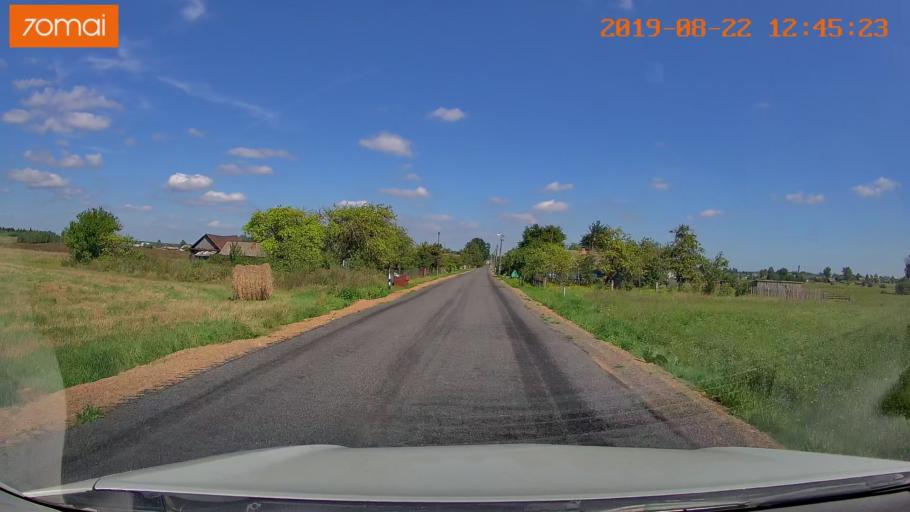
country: BY
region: Minsk
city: Prawdzinski
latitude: 53.4569
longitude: 27.6192
